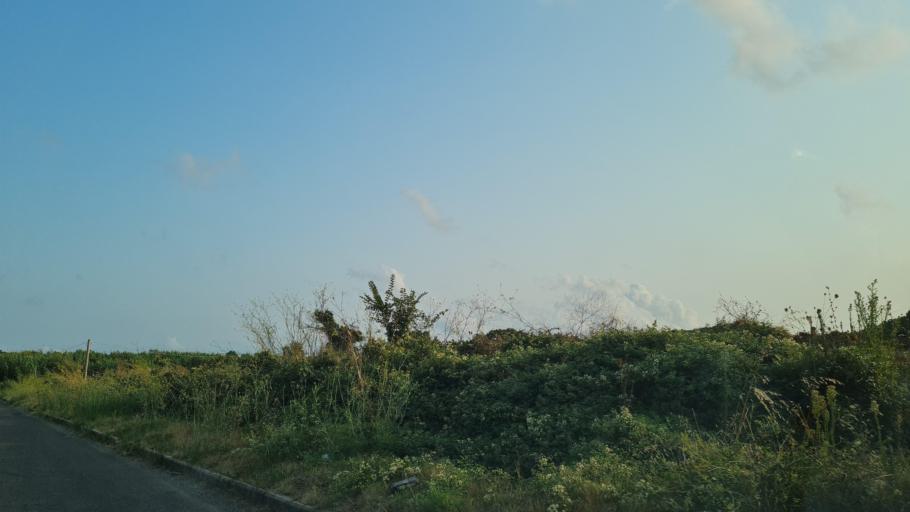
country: IT
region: Latium
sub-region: Provincia di Viterbo
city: Montalto di Castro
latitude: 42.3320
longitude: 11.6145
